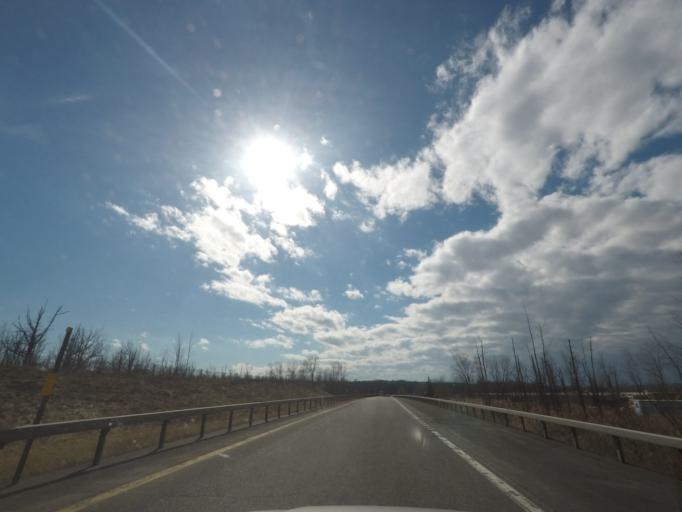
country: US
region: New York
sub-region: Onondaga County
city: East Syracuse
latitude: 43.0585
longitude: -76.0548
